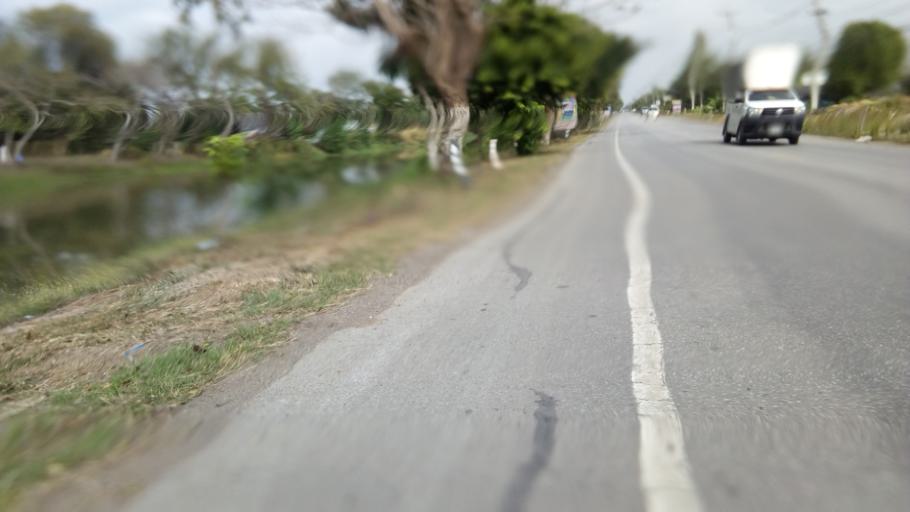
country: TH
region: Pathum Thani
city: Nong Suea
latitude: 14.1463
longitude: 100.8238
